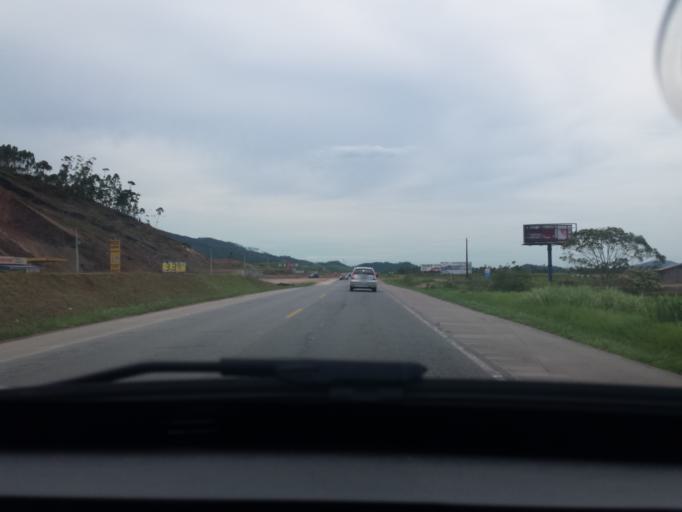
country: BR
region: Santa Catarina
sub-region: Gaspar
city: Gaspar
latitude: -26.8920
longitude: -48.8870
